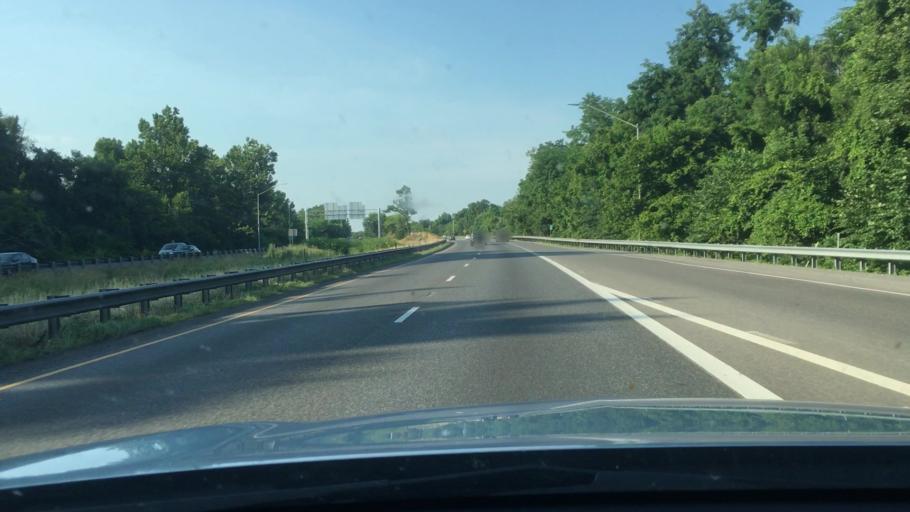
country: US
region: Maryland
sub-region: Washington County
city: Maugansville
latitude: 39.6658
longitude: -77.7379
